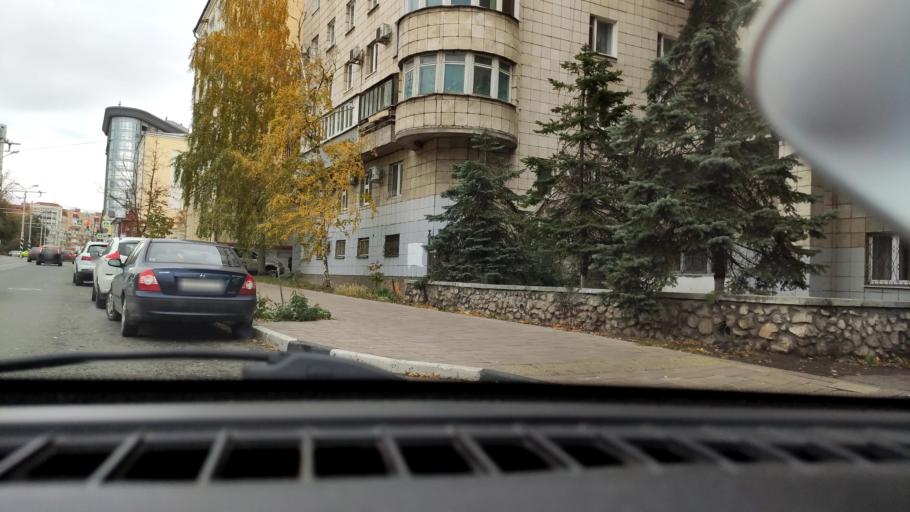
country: RU
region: Samara
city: Samara
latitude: 53.1959
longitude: 50.1051
